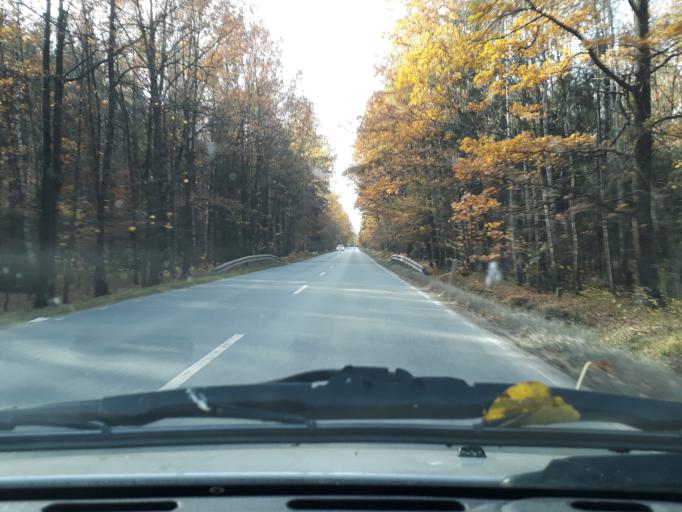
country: PL
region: Silesian Voivodeship
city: Wozniki
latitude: 50.5783
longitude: 19.0353
